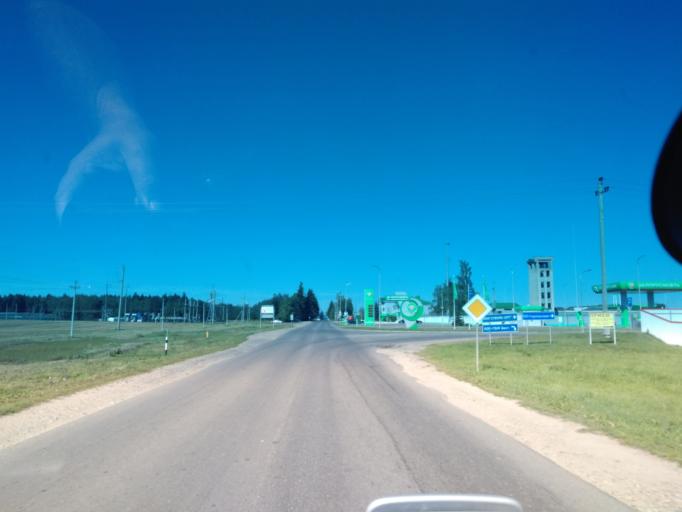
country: BY
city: Fanipol
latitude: 53.7408
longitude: 27.3530
